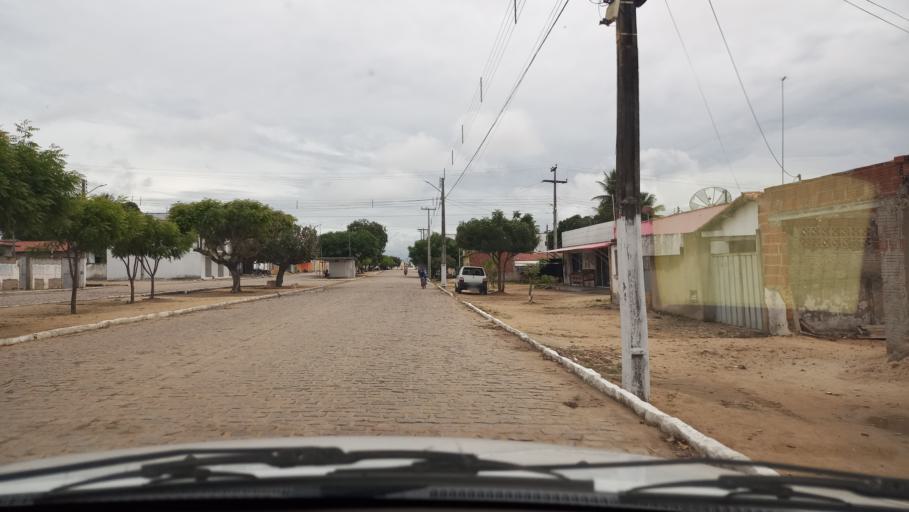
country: BR
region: Rio Grande do Norte
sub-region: Poco Branco
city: Poco Branco
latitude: -5.6202
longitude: -35.6631
